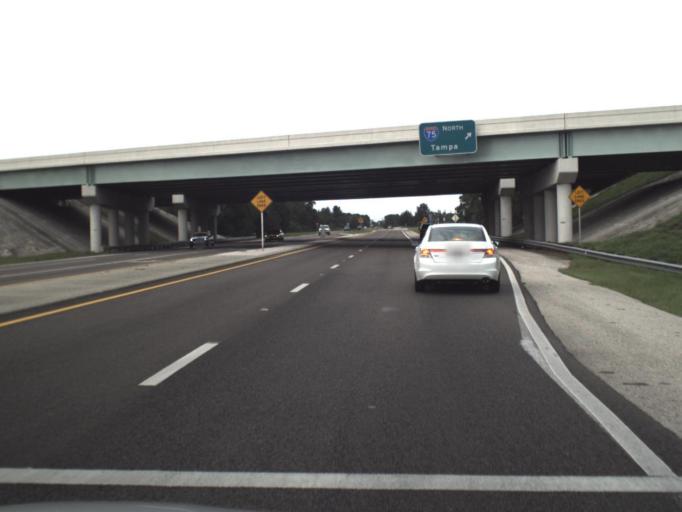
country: US
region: Florida
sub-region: Sarasota County
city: Plantation
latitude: 27.1103
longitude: -82.3843
